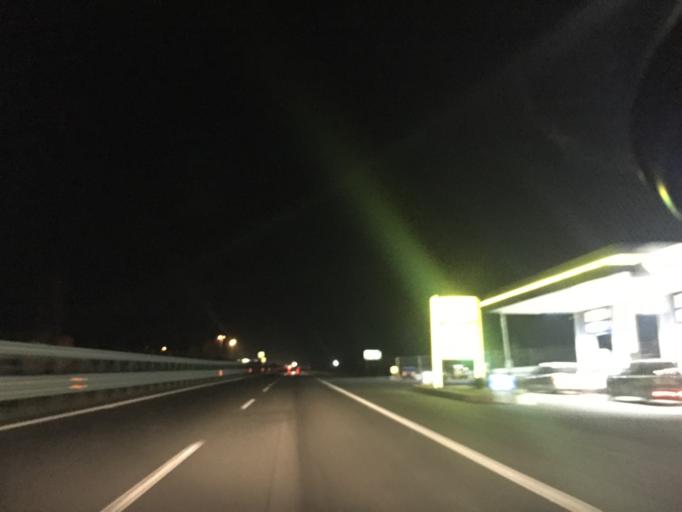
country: AL
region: Lezhe
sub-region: Rrethi i Kurbinit
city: Lac
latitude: 41.6325
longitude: 19.6706
